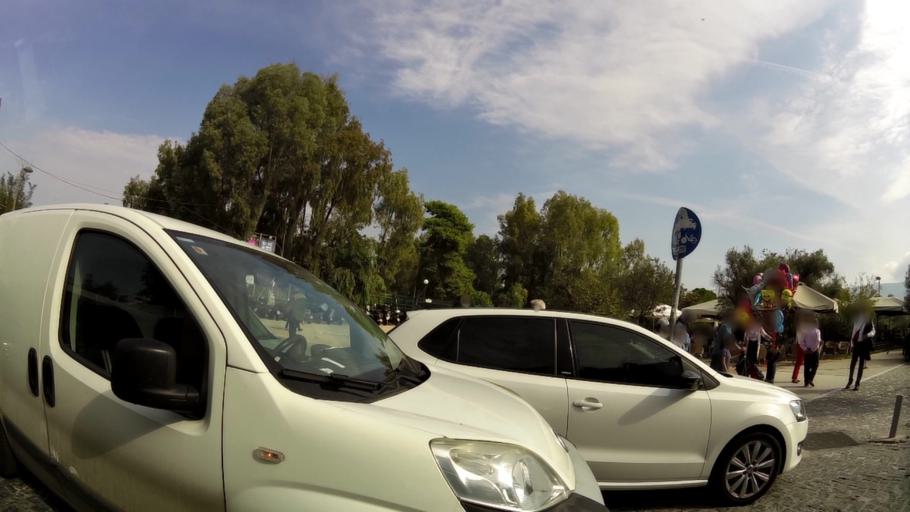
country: GR
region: Attica
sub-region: Nomarchia Athinas
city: Athens
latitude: 37.9745
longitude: 23.7198
